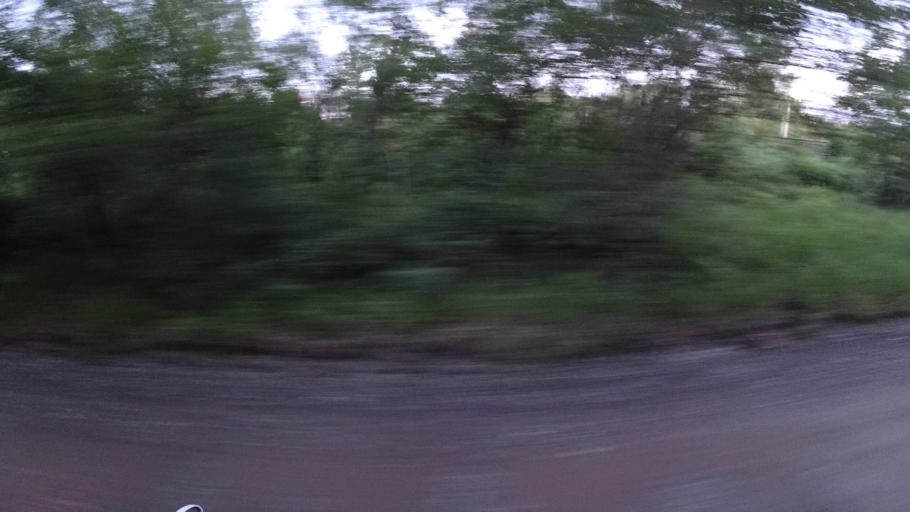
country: RU
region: Khabarovsk Krai
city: Khor
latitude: 47.8503
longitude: 134.9461
